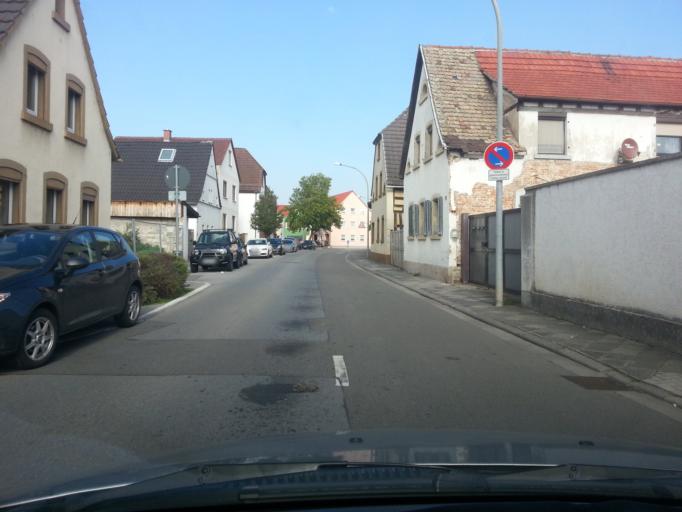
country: DE
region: Rheinland-Pfalz
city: Hassloch
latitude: 49.3615
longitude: 8.2657
